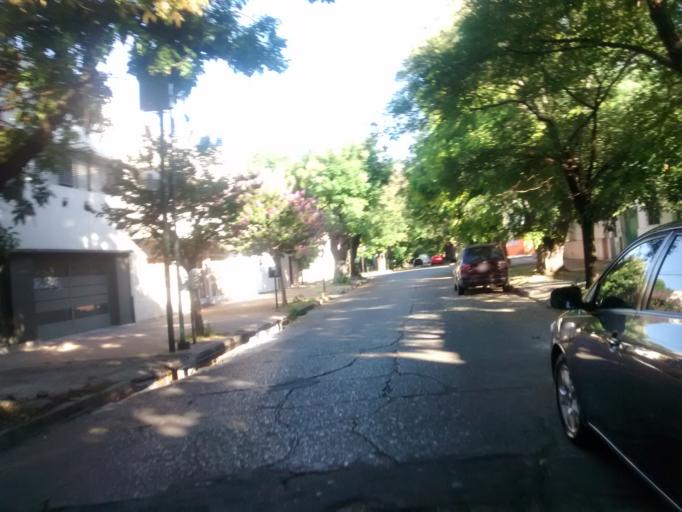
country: AR
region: Buenos Aires
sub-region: Partido de La Plata
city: La Plata
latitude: -34.9244
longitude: -57.9299
